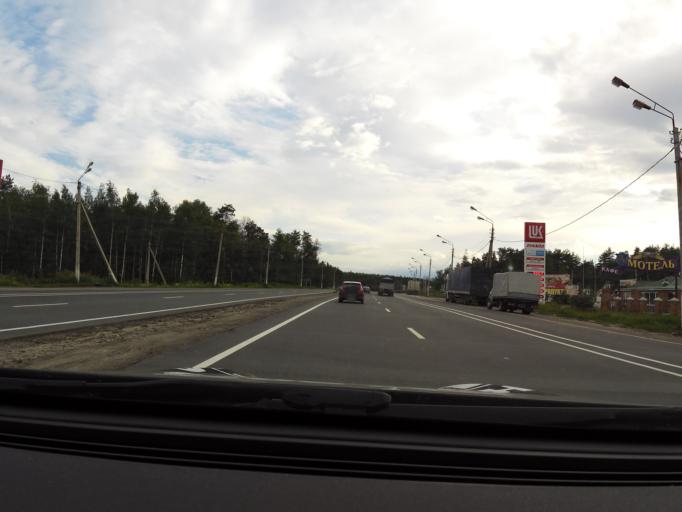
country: RU
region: Vladimir
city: Kommunar
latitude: 56.0628
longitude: 40.4559
